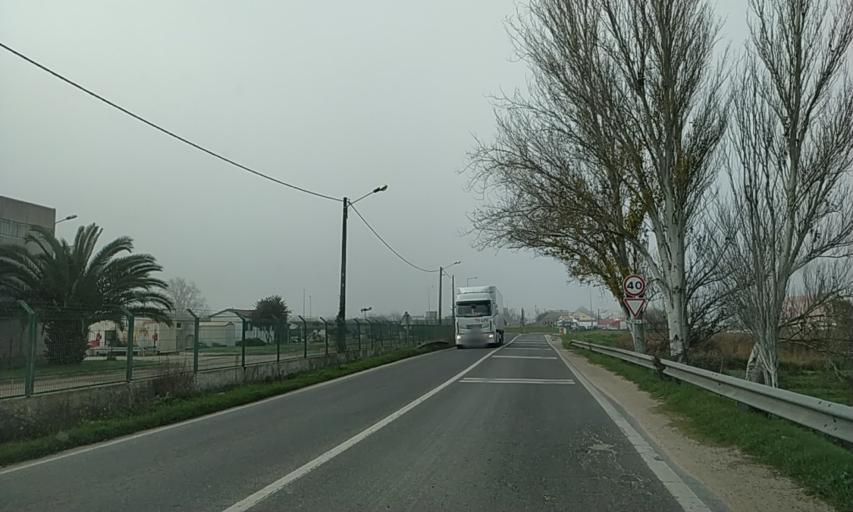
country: PT
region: Setubal
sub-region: Montijo
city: Montijo
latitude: 38.6857
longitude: -8.9476
